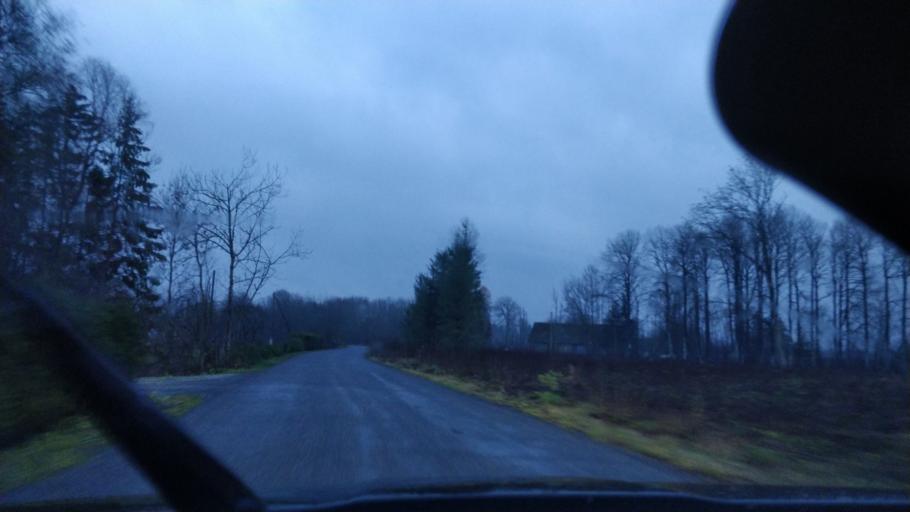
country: EE
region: Laeaene
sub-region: Lihula vald
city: Lihula
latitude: 58.8549
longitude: 24.0105
